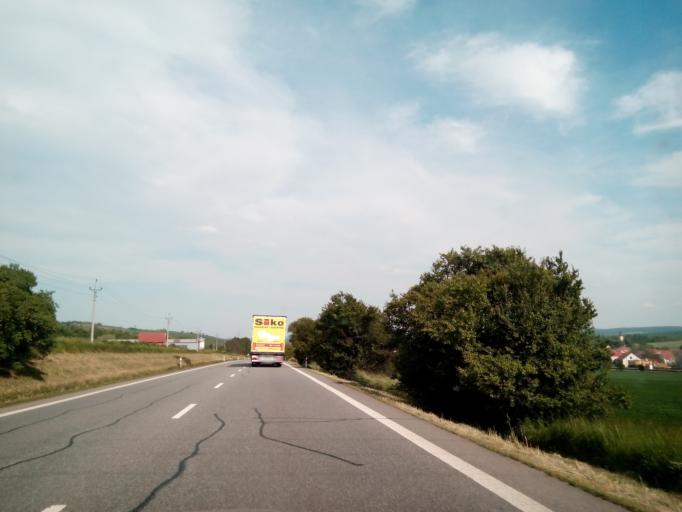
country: CZ
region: South Moravian
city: Letonice
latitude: 49.1477
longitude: 16.9297
